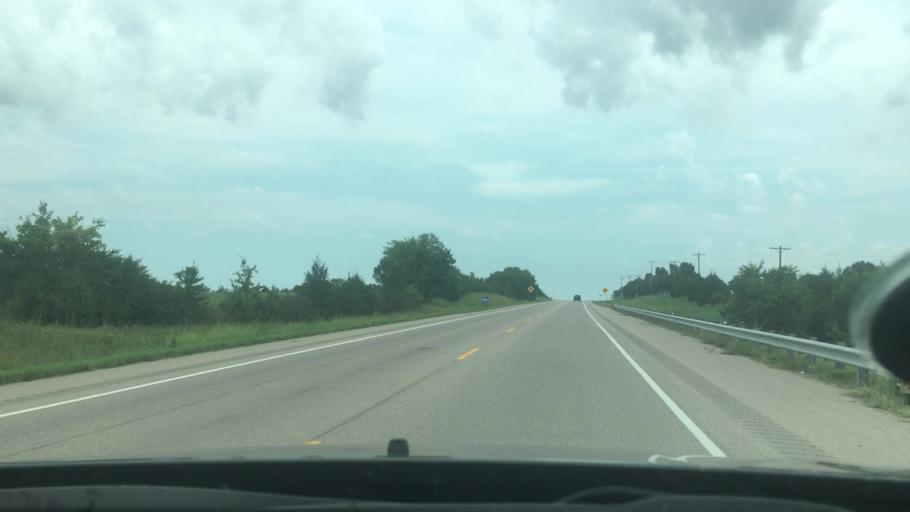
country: US
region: Oklahoma
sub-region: Seminole County
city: Konawa
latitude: 34.9811
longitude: -96.6792
